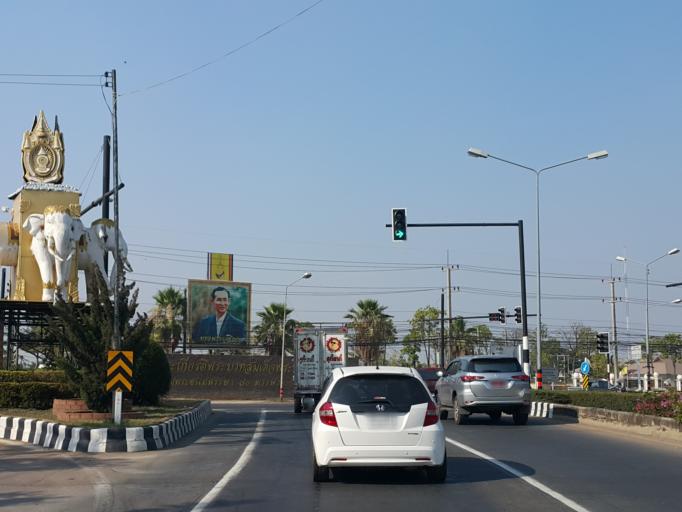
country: TH
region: Phitsanulok
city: Phitsanulok
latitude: 16.8179
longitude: 100.2887
